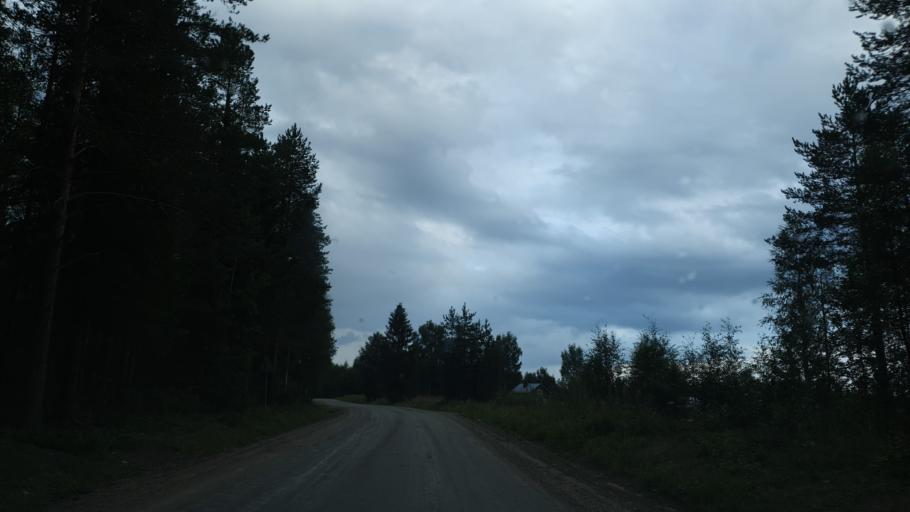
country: FI
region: Kainuu
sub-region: Kehys-Kainuu
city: Kuhmo
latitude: 64.2069
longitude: 29.3712
